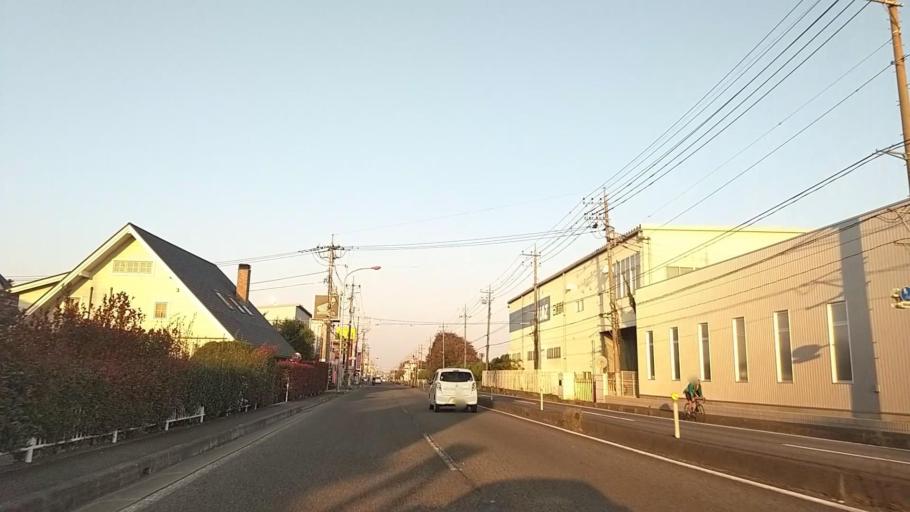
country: JP
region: Saitama
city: Sayama
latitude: 35.8815
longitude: 139.4359
